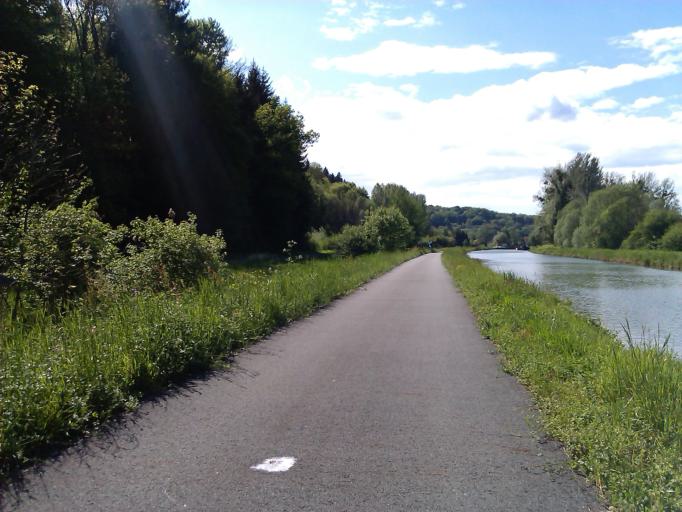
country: FR
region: Franche-Comte
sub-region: Departement du Doubs
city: Colombier-Fontaine
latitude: 47.4267
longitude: 6.6179
